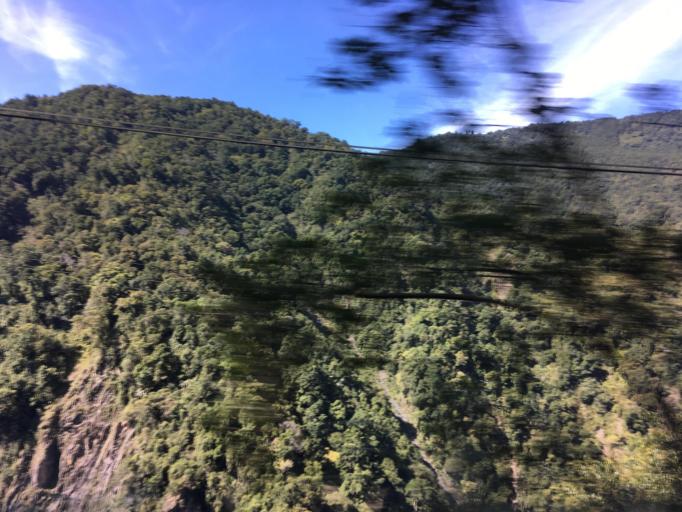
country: TW
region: Taiwan
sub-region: Yilan
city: Yilan
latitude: 24.5561
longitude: 121.5020
